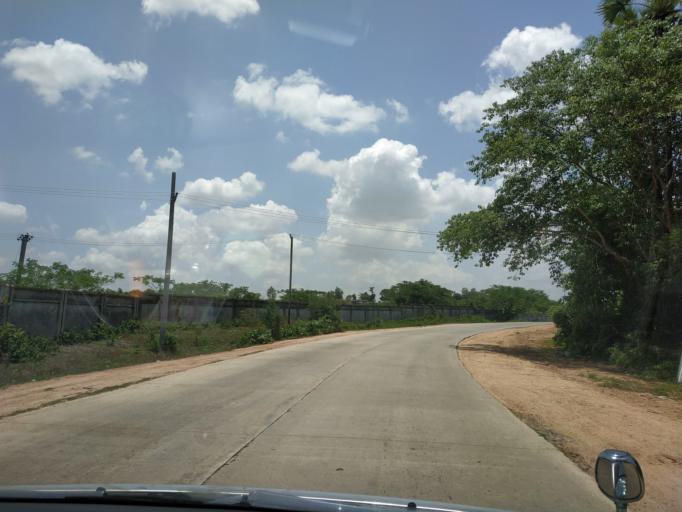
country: MM
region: Bago
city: Bago
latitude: 17.4699
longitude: 96.4568
